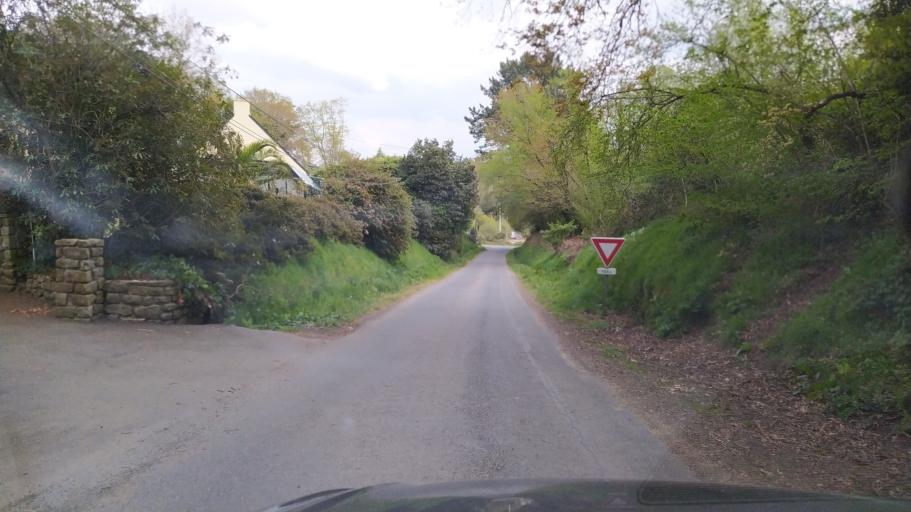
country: FR
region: Brittany
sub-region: Departement du Finistere
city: Bodilis
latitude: 48.5001
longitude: -4.1015
